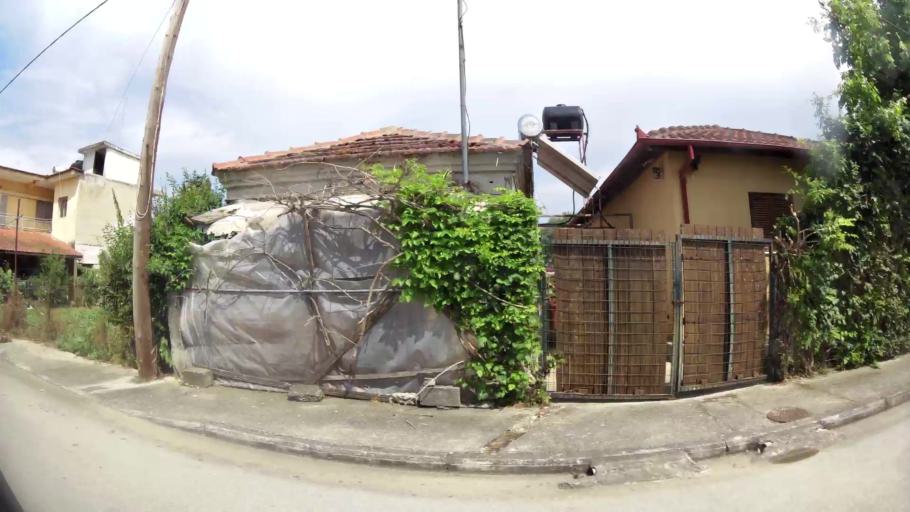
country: GR
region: Central Macedonia
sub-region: Nomos Pierias
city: Korinos
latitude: 40.3214
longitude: 22.5876
